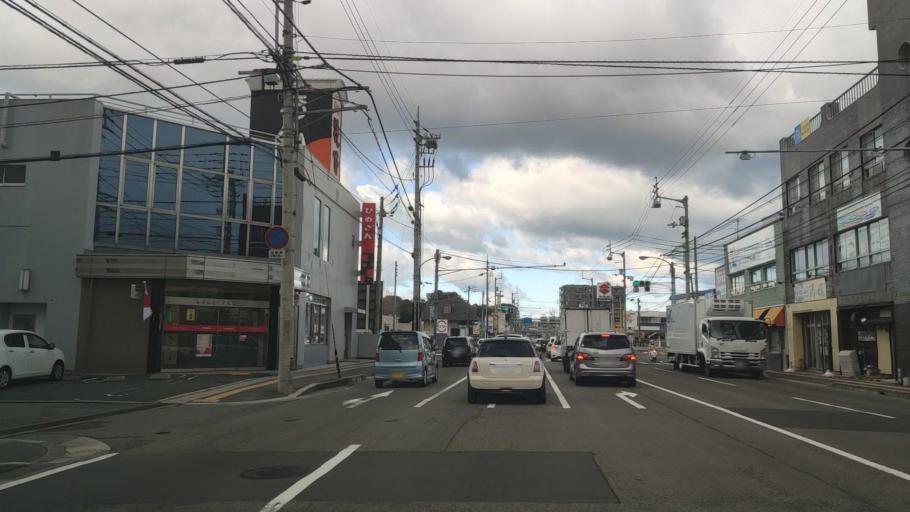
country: JP
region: Ehime
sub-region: Shikoku-chuo Shi
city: Matsuyama
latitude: 33.8549
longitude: 132.7487
